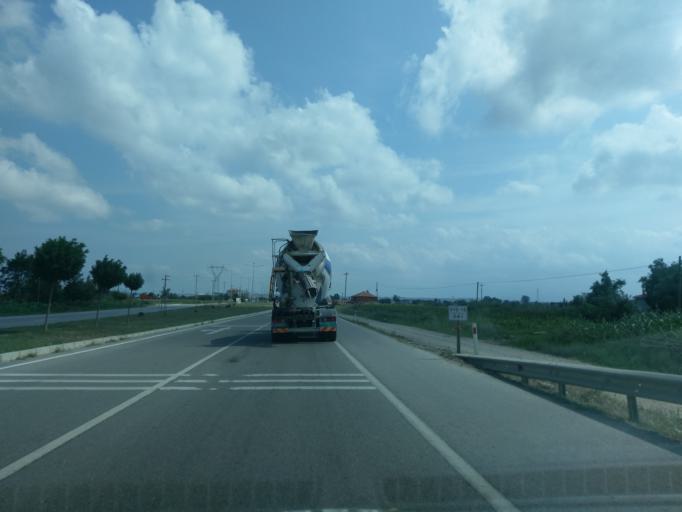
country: TR
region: Samsun
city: Bafra
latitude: 41.5785
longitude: 35.8500
